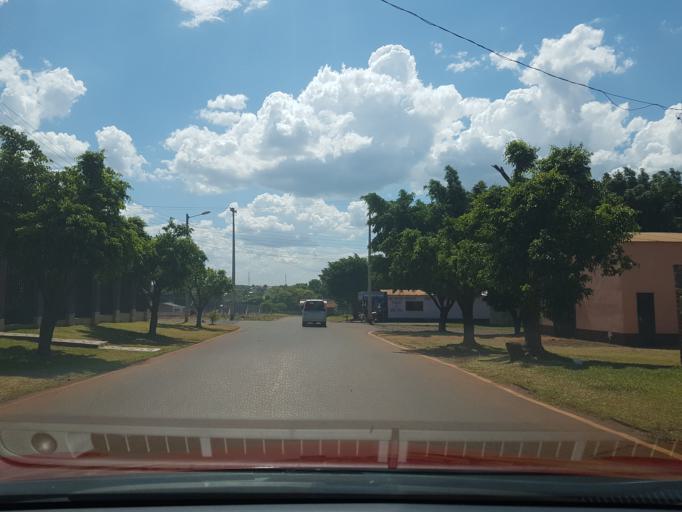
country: PY
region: Alto Parana
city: Ciudad del Este
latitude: -25.4824
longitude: -54.6809
